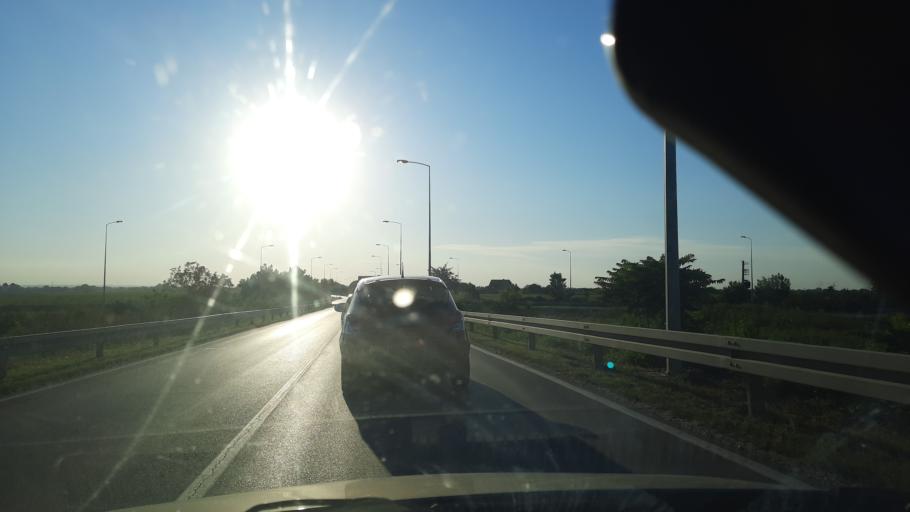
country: RS
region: Central Serbia
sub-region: Branicevski Okrug
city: Pozarevac
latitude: 44.5995
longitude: 21.1487
